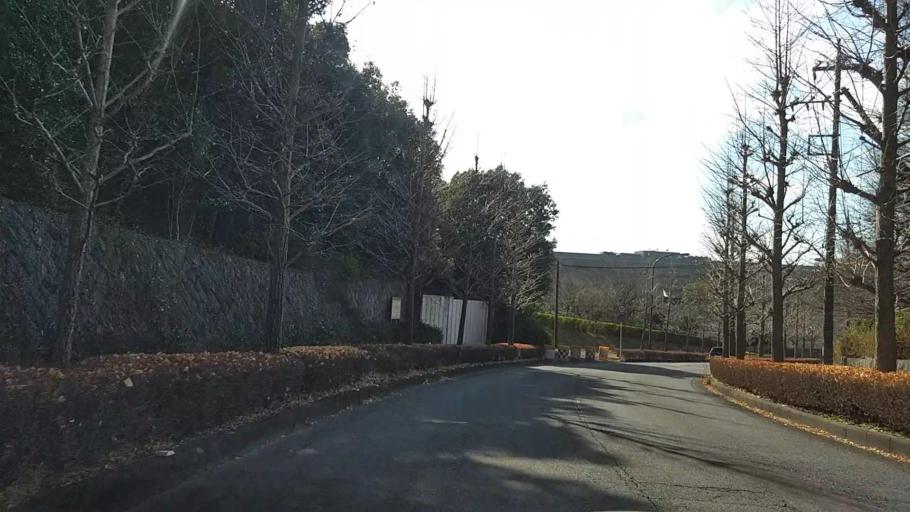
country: JP
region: Kanagawa
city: Atsugi
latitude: 35.4429
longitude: 139.3172
